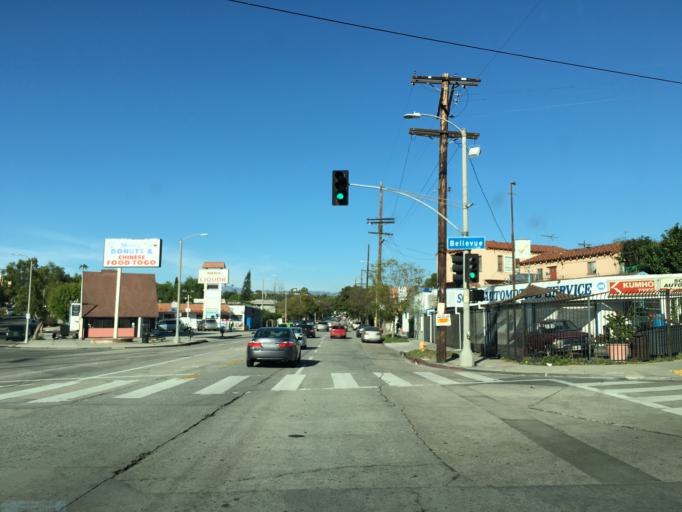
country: US
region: California
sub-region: Los Angeles County
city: Silver Lake
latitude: 34.0783
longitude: -118.2791
